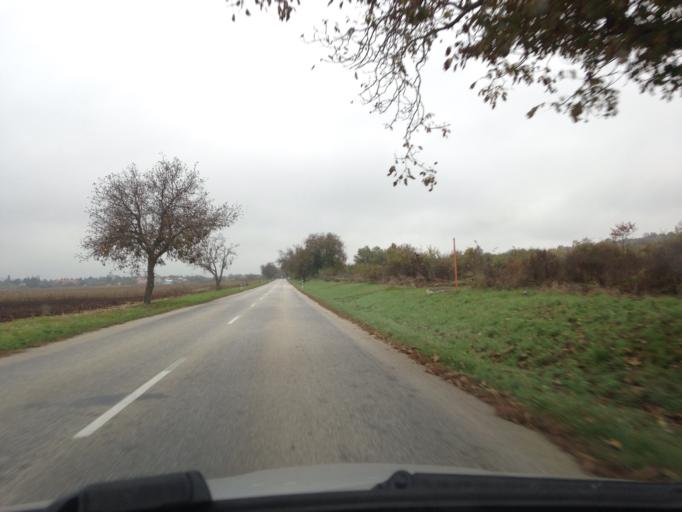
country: SK
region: Nitriansky
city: Svodin
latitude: 47.8407
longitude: 18.5355
